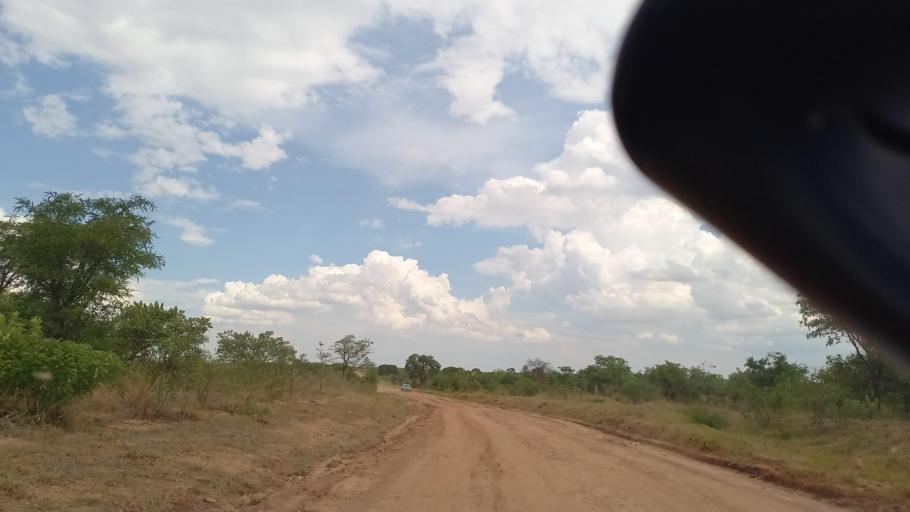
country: ZM
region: Southern
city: Nakambala
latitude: -16.0623
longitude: 27.9938
